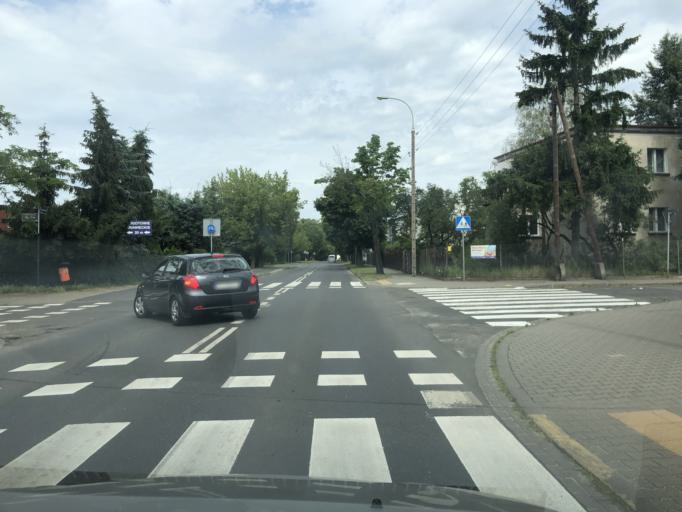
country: PL
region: Greater Poland Voivodeship
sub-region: Powiat poznanski
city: Lubon
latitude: 52.3601
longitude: 16.8808
